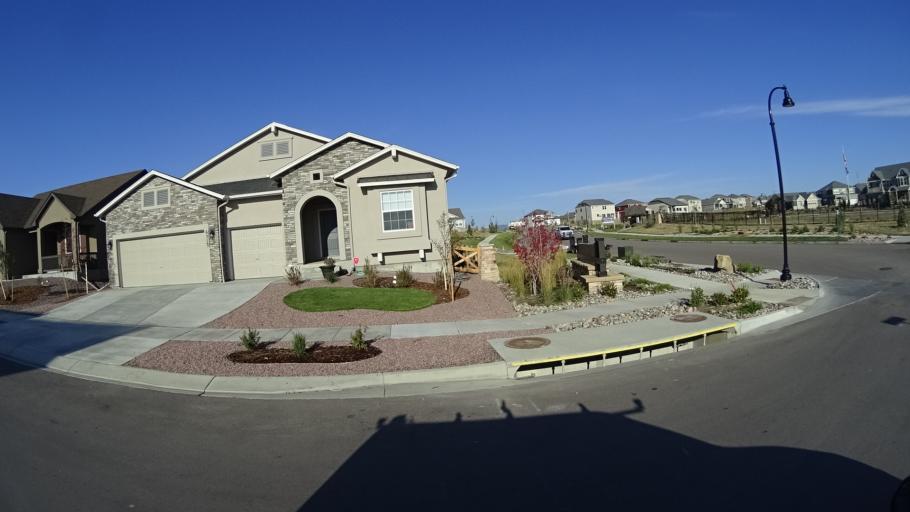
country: US
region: Colorado
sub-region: El Paso County
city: Cimarron Hills
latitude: 38.9311
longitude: -104.6537
